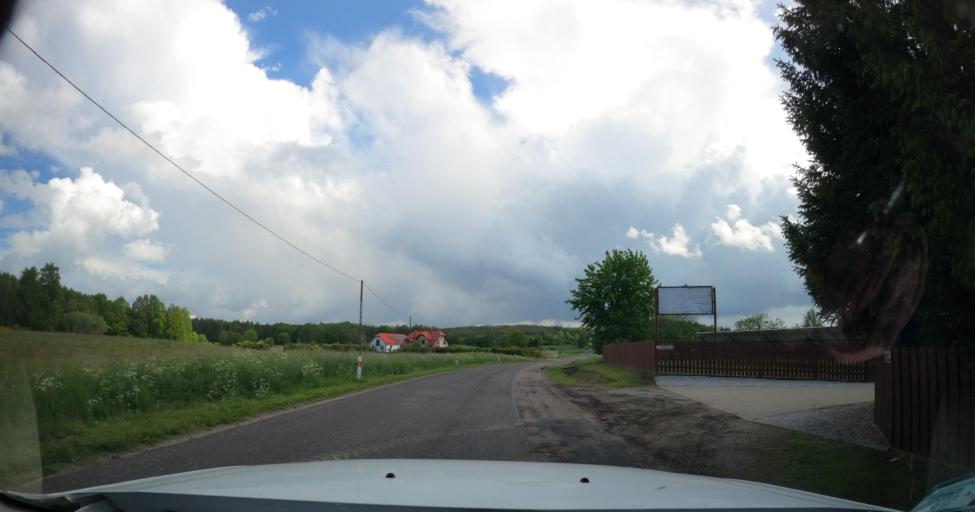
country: PL
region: Pomeranian Voivodeship
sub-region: Powiat bytowski
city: Czarna Dabrowka
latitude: 54.3538
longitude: 17.5739
